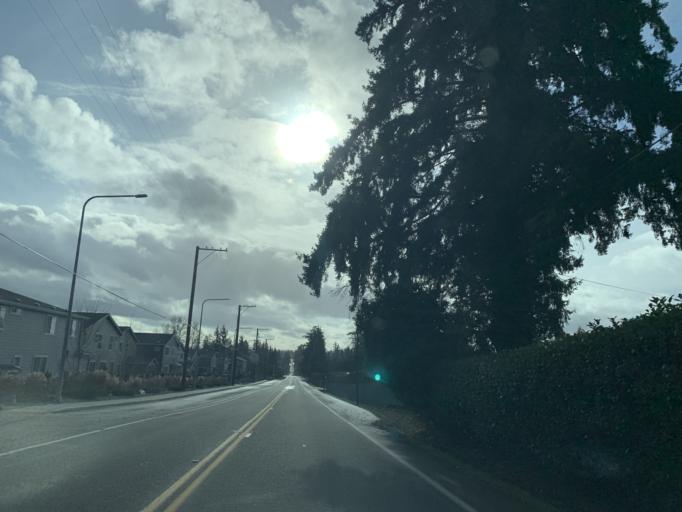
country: US
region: Washington
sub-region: King County
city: Lakeland South
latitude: 47.2683
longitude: -122.2979
